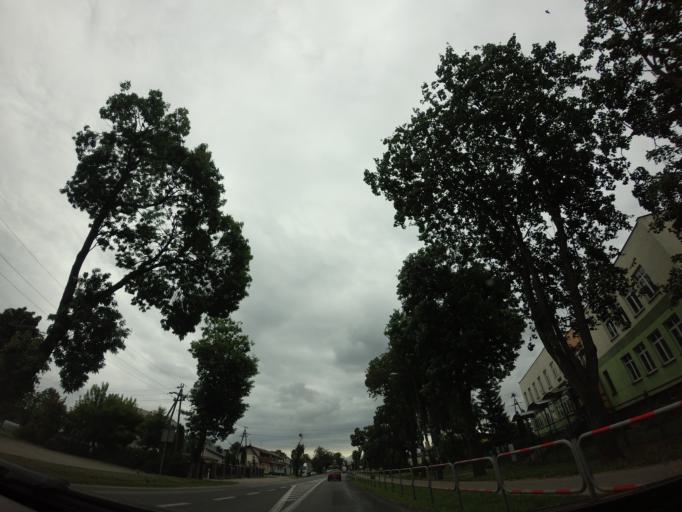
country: PL
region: Masovian Voivodeship
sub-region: Powiat ciechanowski
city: Glinojeck
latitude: 52.8185
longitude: 20.2881
